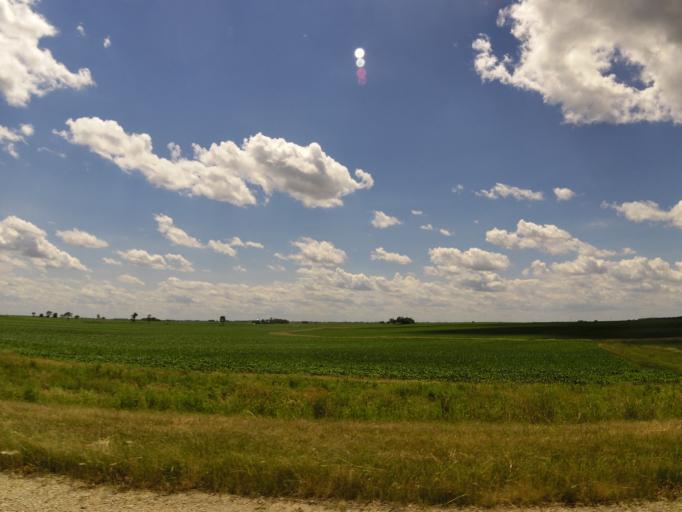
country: US
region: Iowa
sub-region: Buchanan County
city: Independence
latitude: 42.5389
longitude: -91.8913
